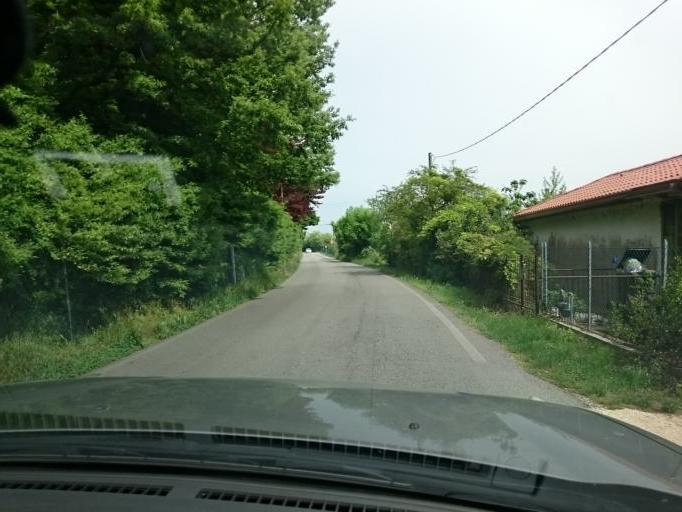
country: IT
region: Veneto
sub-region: Provincia di Venezia
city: Dolo
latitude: 45.4195
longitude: 12.0665
